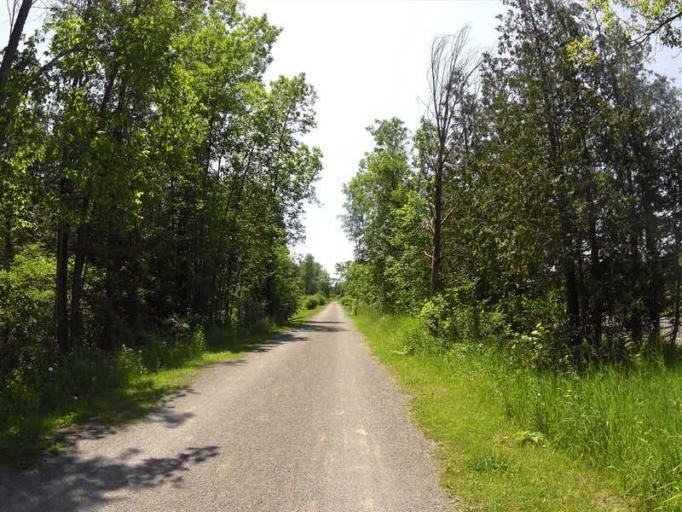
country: CA
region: Ontario
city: Peterborough
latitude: 44.4125
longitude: -78.2624
